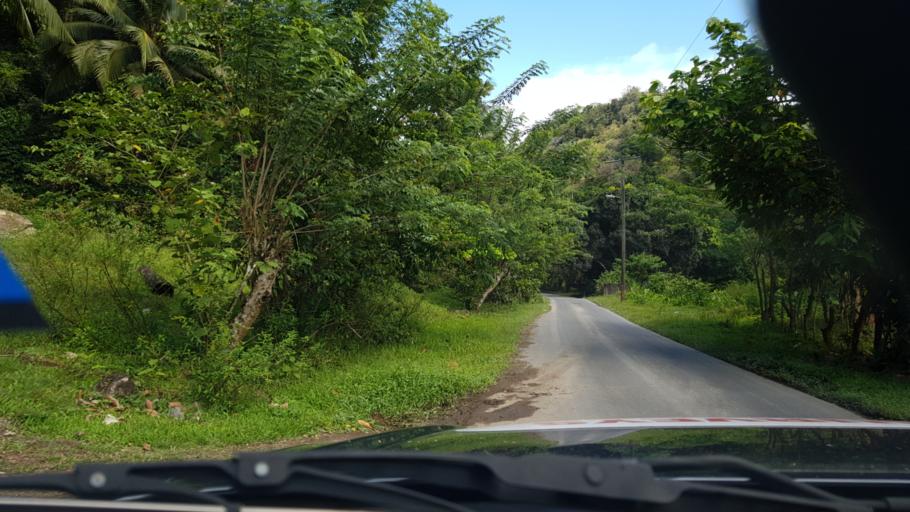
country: LC
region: Anse-la-Raye
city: Anse La Raye
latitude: 13.9356
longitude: -61.0405
